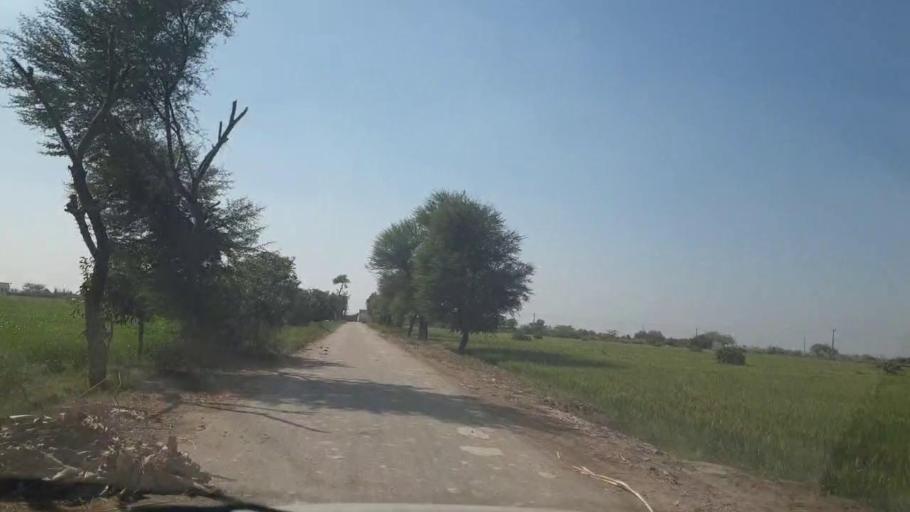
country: PK
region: Sindh
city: Mirpur Khas
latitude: 25.4596
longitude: 69.1768
